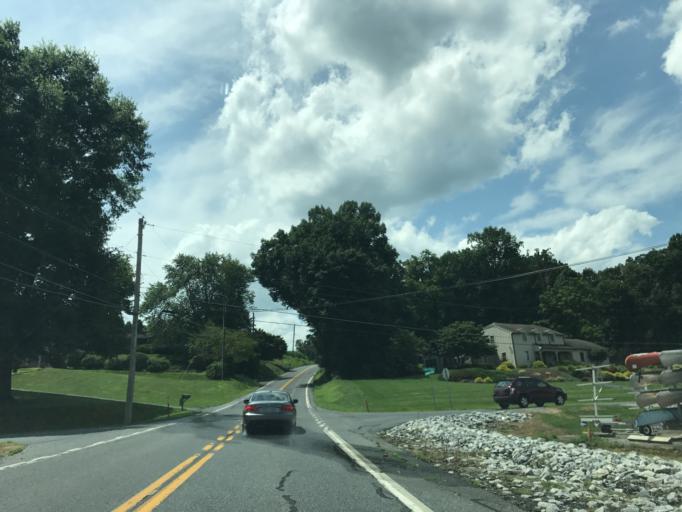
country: US
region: Pennsylvania
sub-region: Lancaster County
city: Brickerville
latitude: 40.2092
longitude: -76.3181
